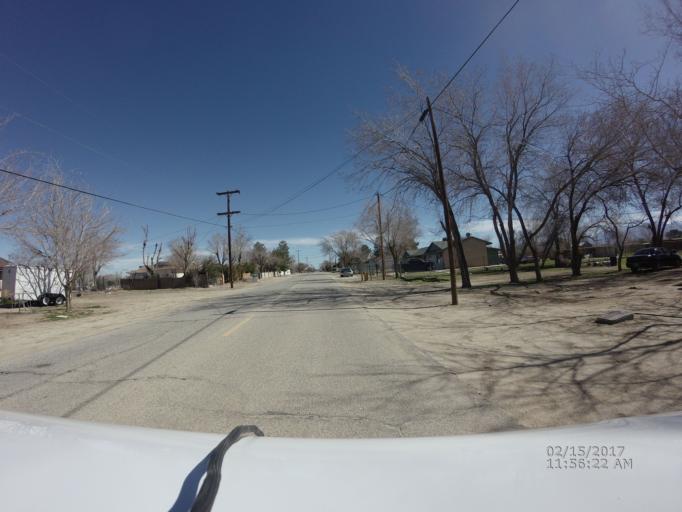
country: US
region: California
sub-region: Los Angeles County
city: Littlerock
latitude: 34.5743
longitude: -117.9546
